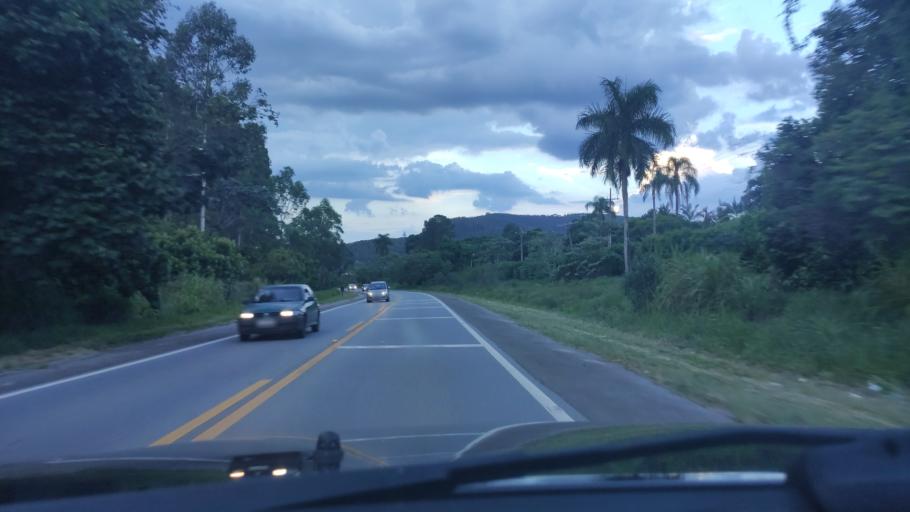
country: BR
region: Sao Paulo
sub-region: Braganca Paulista
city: Braganca Paulista
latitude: -22.8764
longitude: -46.5344
